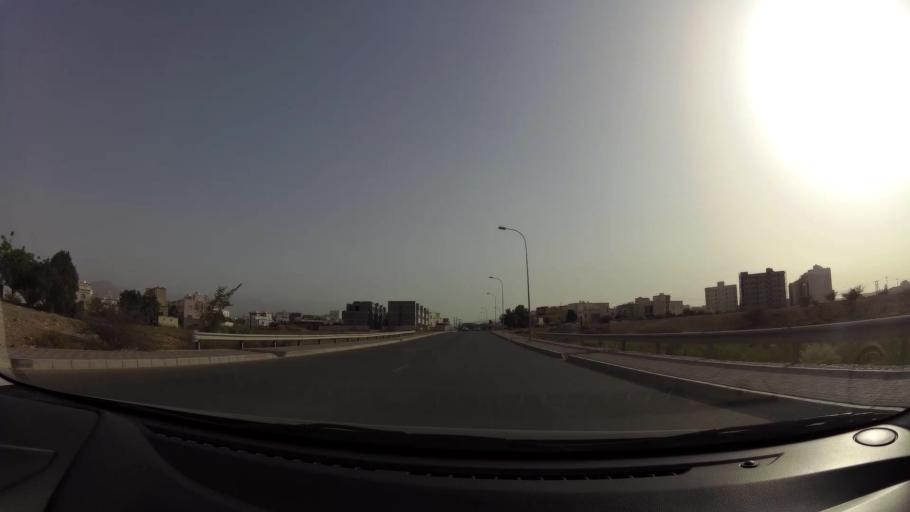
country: OM
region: Muhafazat Masqat
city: Bawshar
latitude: 23.5460
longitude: 58.3603
